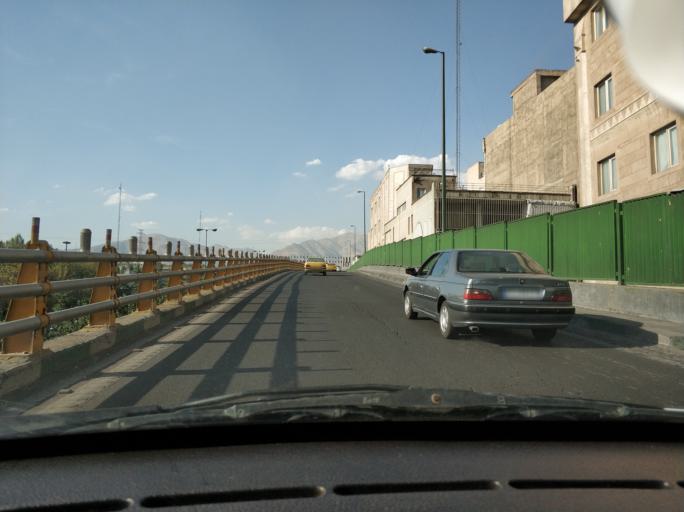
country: IR
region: Tehran
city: Tehran
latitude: 35.7367
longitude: 51.3711
